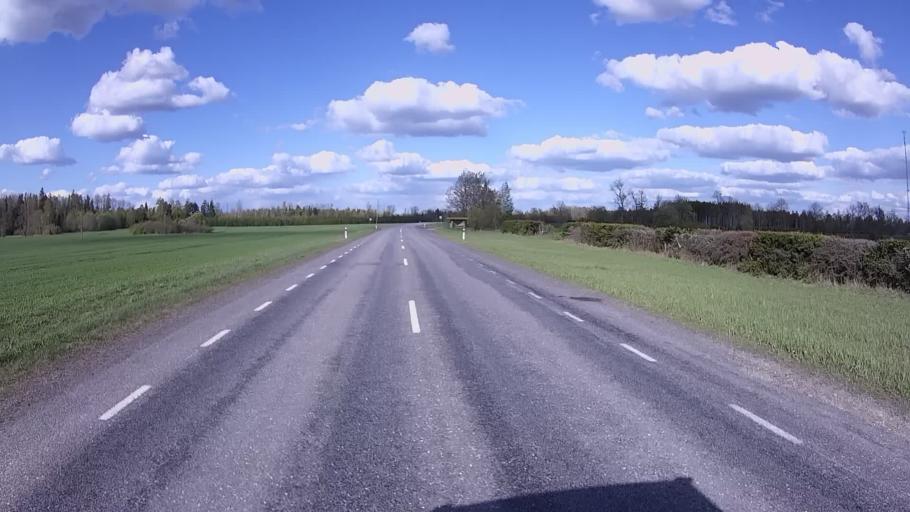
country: EE
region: Jogevamaa
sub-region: Poltsamaa linn
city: Poltsamaa
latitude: 58.6992
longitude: 26.1433
